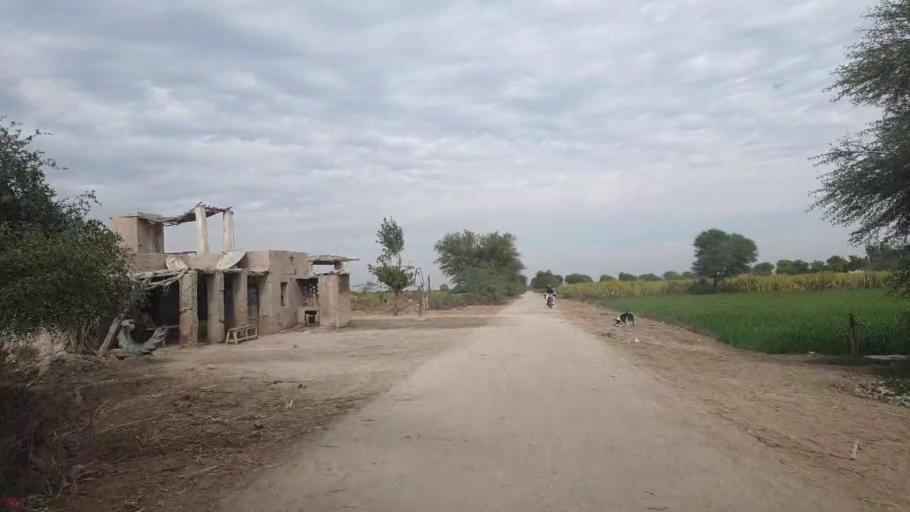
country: PK
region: Sindh
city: Jhol
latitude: 26.0092
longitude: 68.8710
